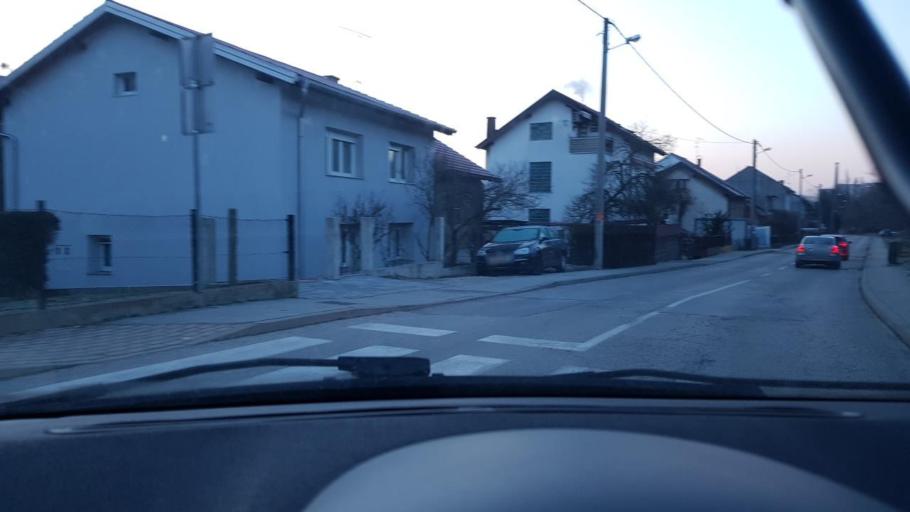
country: HR
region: Grad Zagreb
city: Zagreb
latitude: 45.8322
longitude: 16.0047
